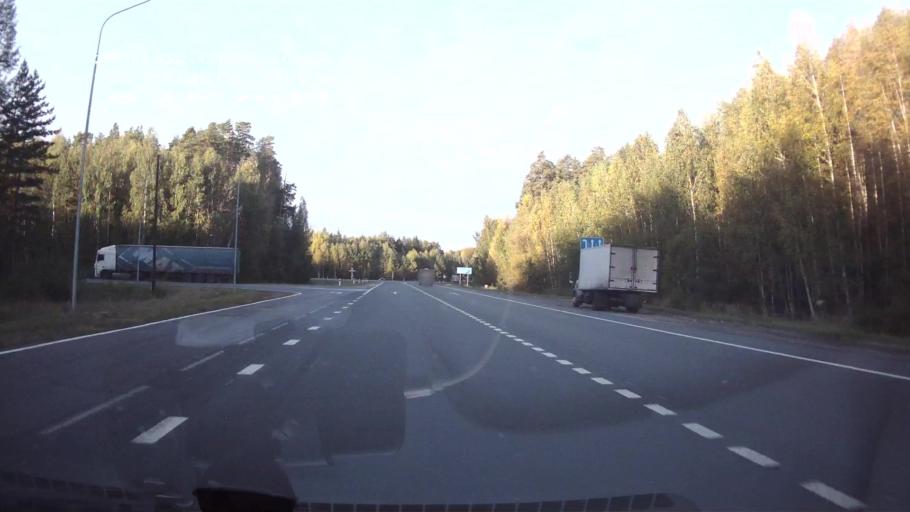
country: RU
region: Chuvashia
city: Mariinskiy Posad
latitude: 56.1903
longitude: 47.7900
